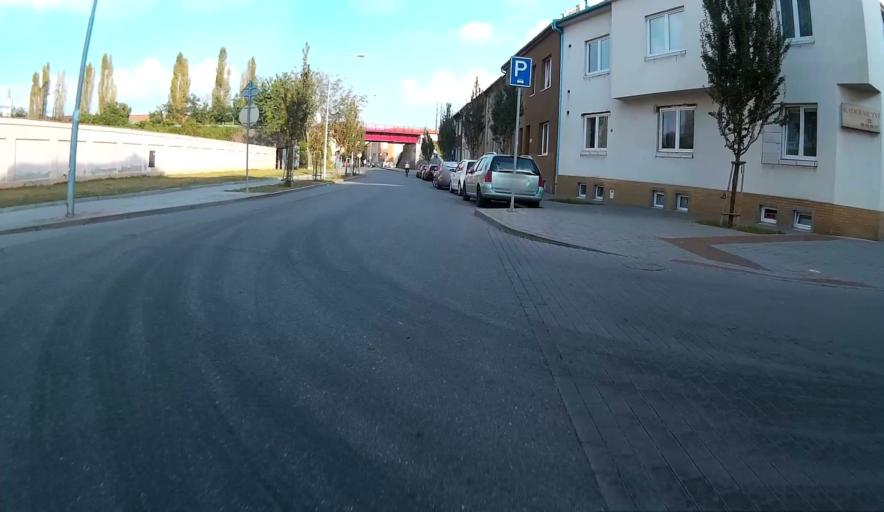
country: CZ
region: South Moravian
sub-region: Mesto Brno
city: Brno
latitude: 49.1959
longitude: 16.6366
